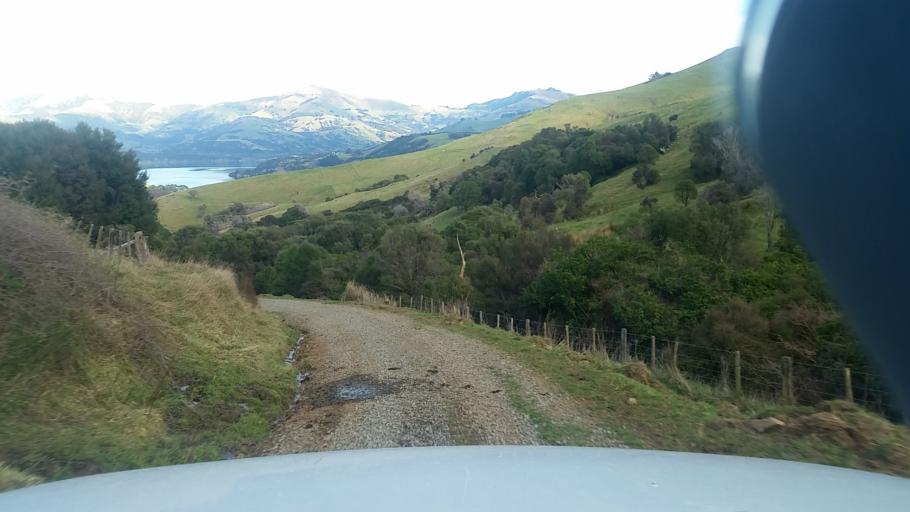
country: NZ
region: Canterbury
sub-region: Christchurch City
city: Christchurch
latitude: -43.7562
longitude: 173.0011
